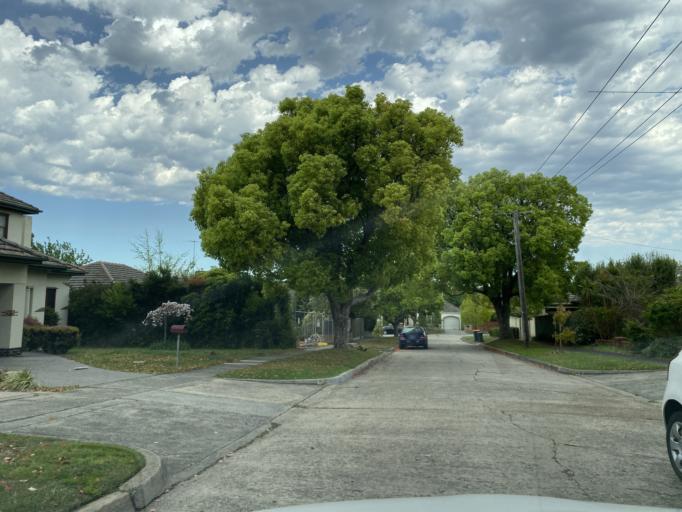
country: AU
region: Victoria
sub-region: Boroondara
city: Canterbury
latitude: -37.8312
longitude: 145.0762
